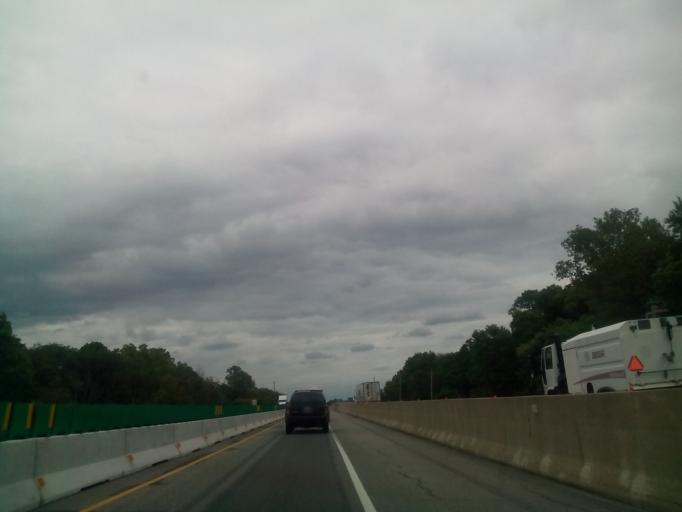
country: US
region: Ohio
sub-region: Lorain County
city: Elyria
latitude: 41.3913
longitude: -82.1338
